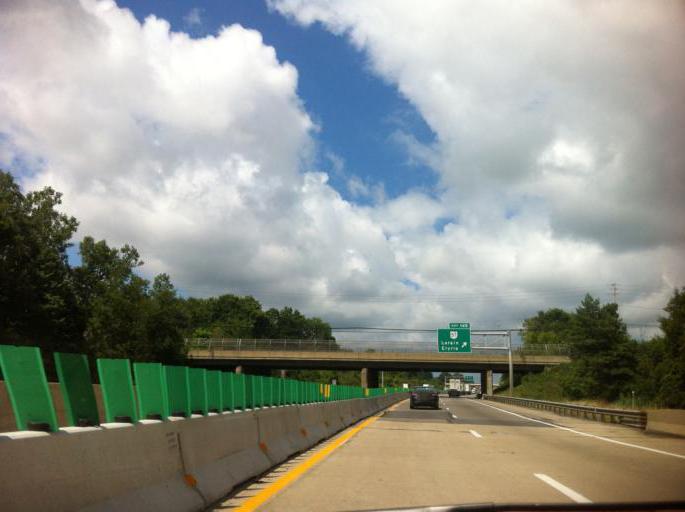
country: US
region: Ohio
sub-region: Lorain County
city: Elyria
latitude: 41.3847
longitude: -82.1038
